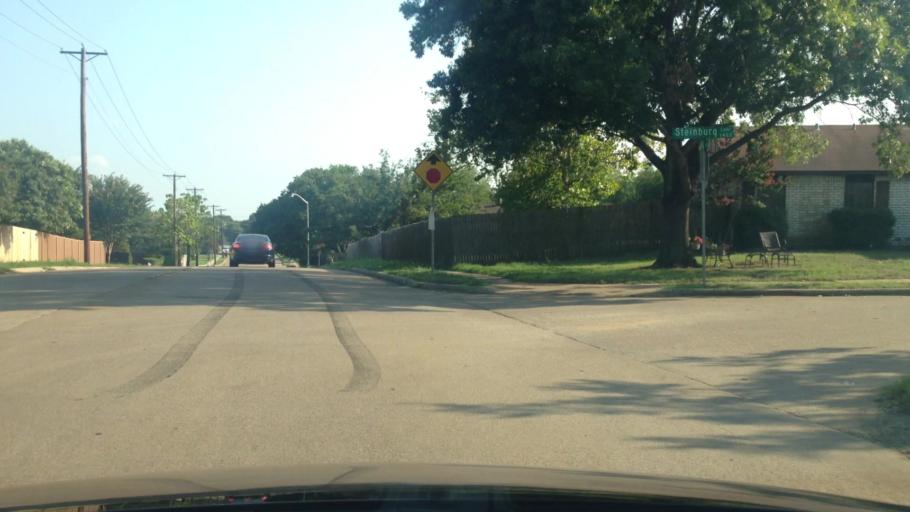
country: US
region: Texas
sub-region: Tarrant County
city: Edgecliff Village
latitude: 32.6453
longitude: -97.3404
